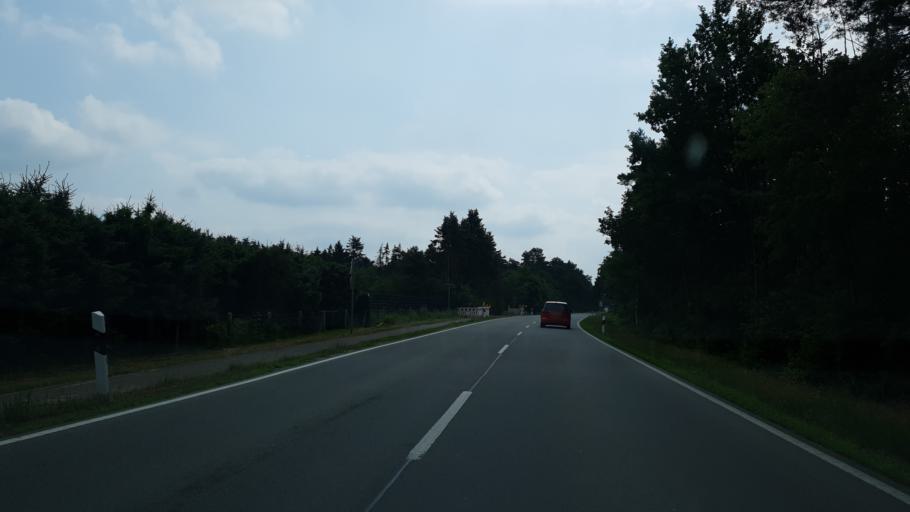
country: DE
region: Lower Saxony
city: Geeste
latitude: 52.5637
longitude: 7.2036
